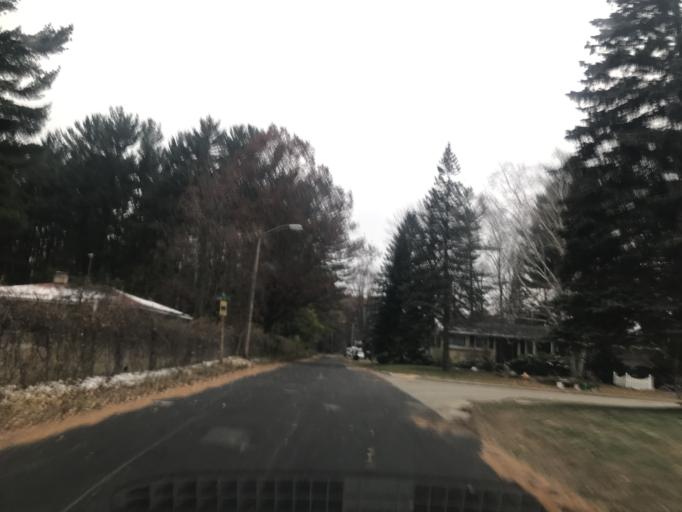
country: US
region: Wisconsin
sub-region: Marinette County
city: Marinette
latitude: 45.0964
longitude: -87.6530
